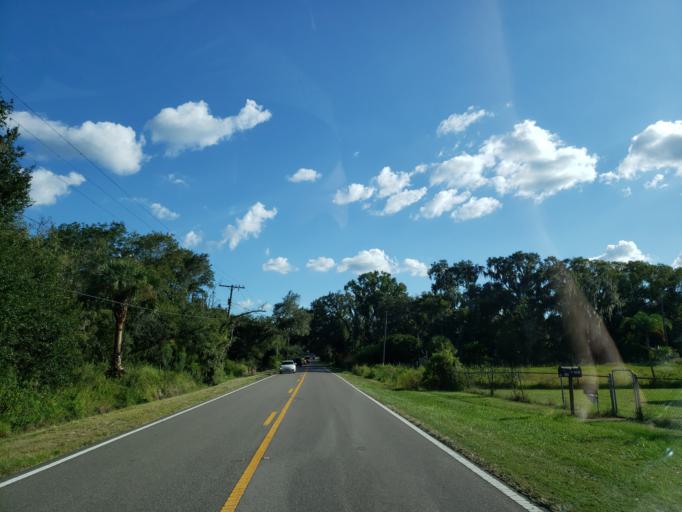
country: US
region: Florida
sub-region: Hillsborough County
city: Valrico
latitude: 27.9471
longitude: -82.2196
